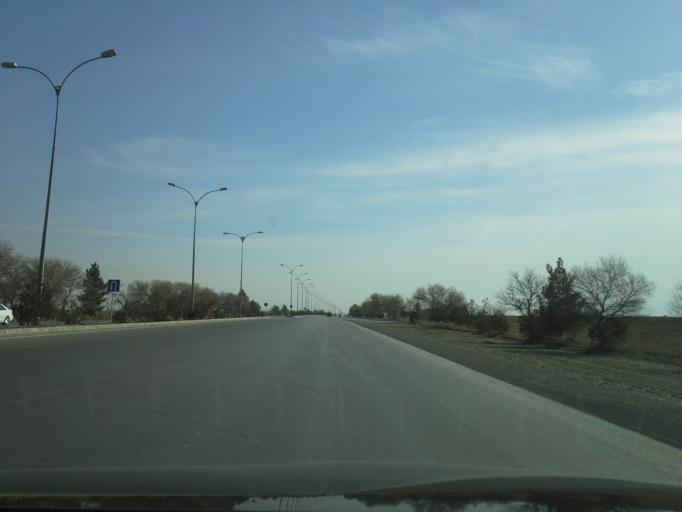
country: TM
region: Ahal
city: Abadan
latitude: 38.1251
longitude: 58.0337
